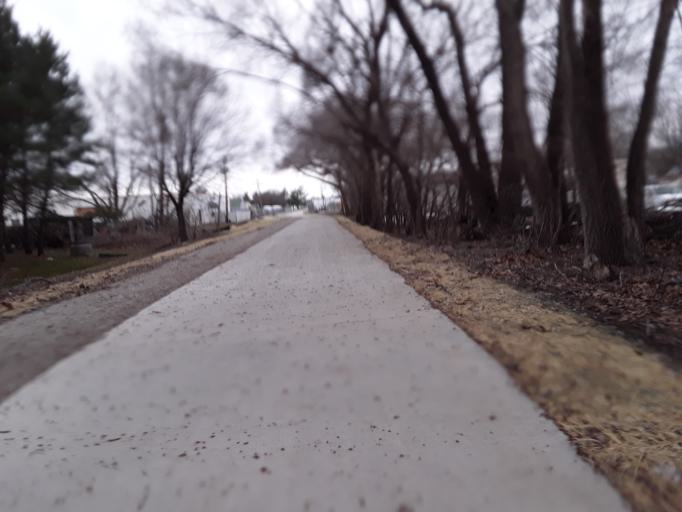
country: US
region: Nebraska
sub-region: Lancaster County
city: Lincoln
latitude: 40.8514
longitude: -96.6368
